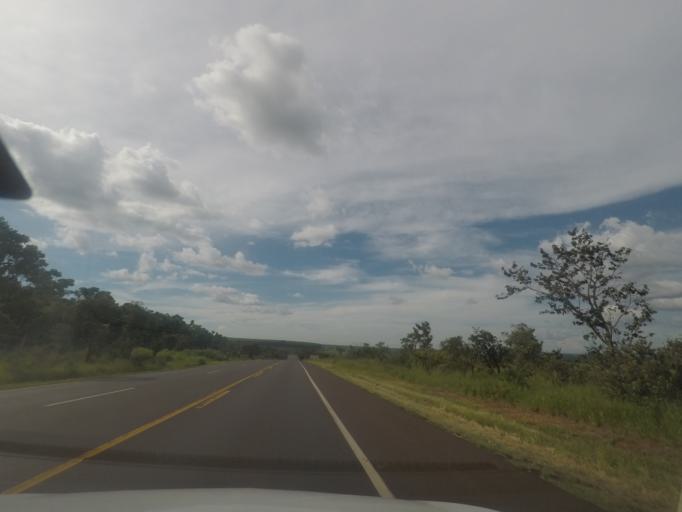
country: BR
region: Minas Gerais
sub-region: Prata
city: Prata
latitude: -19.1453
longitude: -48.9635
